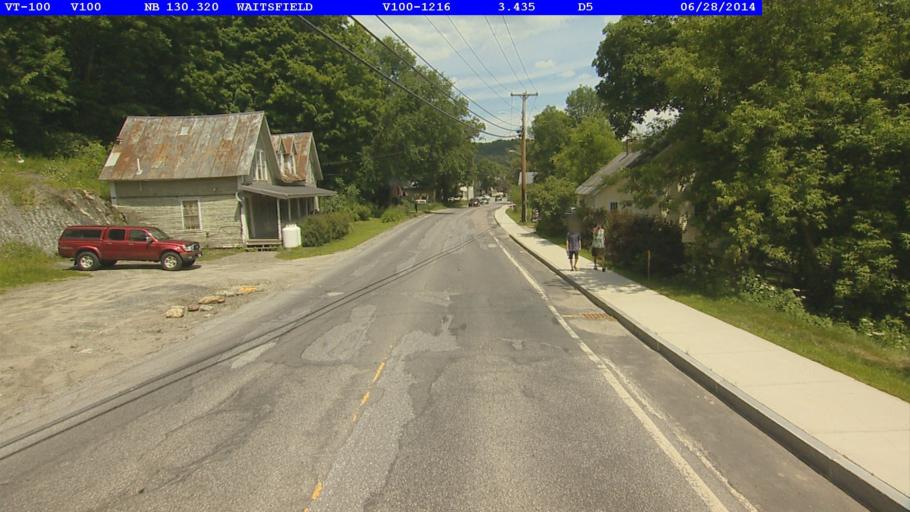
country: US
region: Vermont
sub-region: Washington County
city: Waterbury
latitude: 44.1888
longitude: -72.8281
